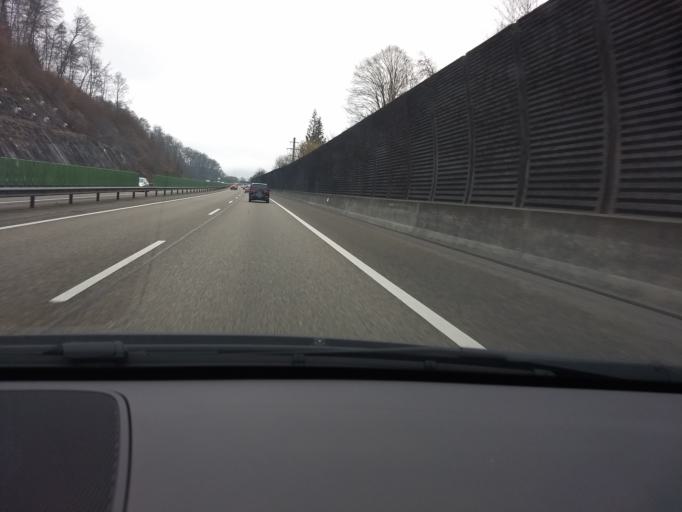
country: CH
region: Basel-Landschaft
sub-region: Bezirk Sissach
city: Tenniken
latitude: 47.4372
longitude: 7.8087
